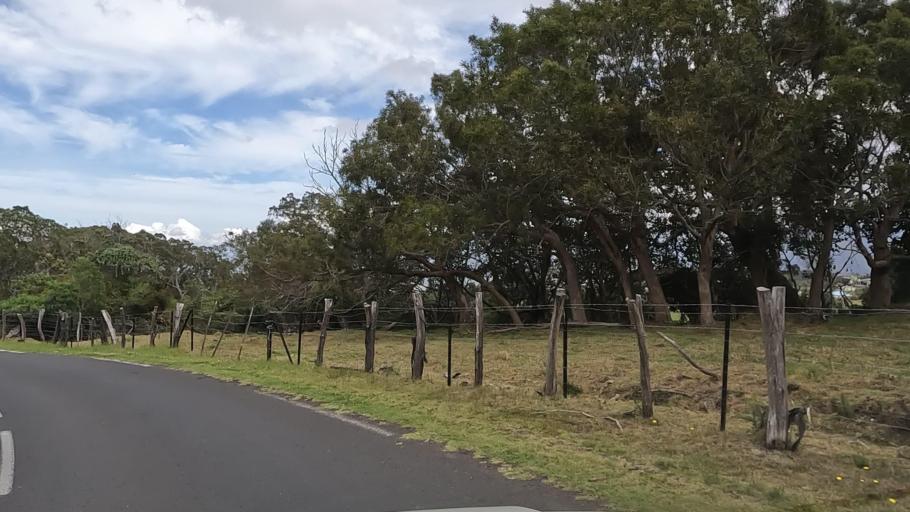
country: RE
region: Reunion
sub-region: Reunion
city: Le Tampon
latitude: -21.2396
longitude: 55.5857
